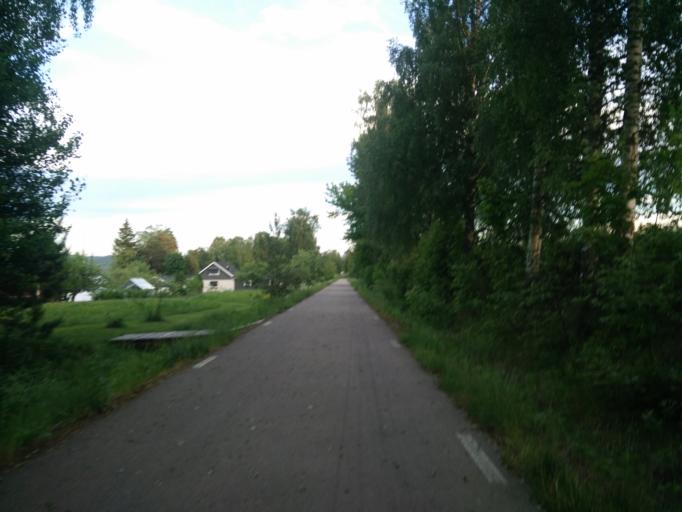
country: SE
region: Vaermland
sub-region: Hagfors Kommun
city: Hagfors
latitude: 60.0093
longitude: 13.6015
